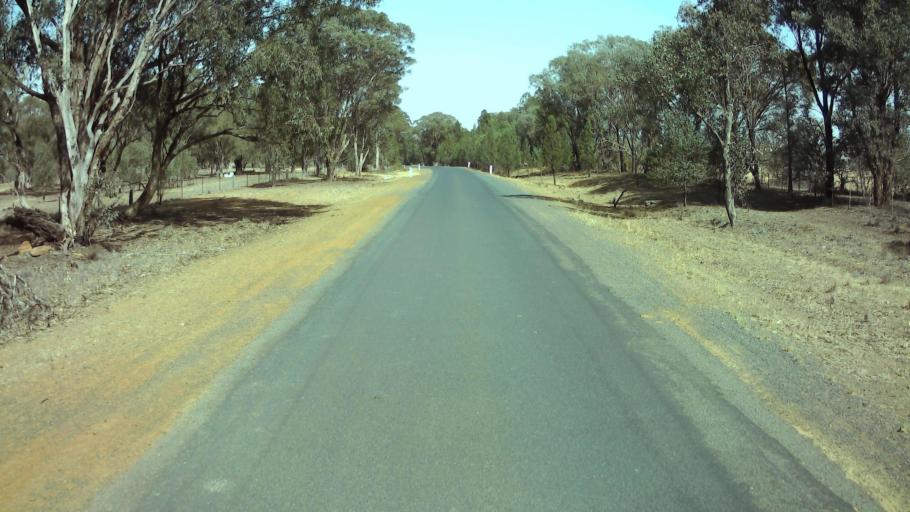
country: AU
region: New South Wales
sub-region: Weddin
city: Grenfell
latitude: -33.8691
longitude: 148.0819
